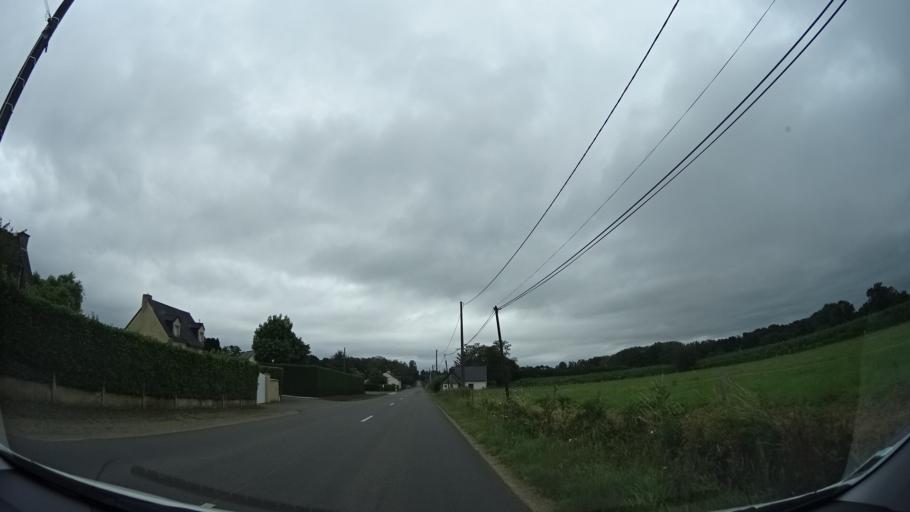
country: FR
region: Brittany
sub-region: Departement d'Ille-et-Vilaine
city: Meillac
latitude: 48.3953
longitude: -1.7840
